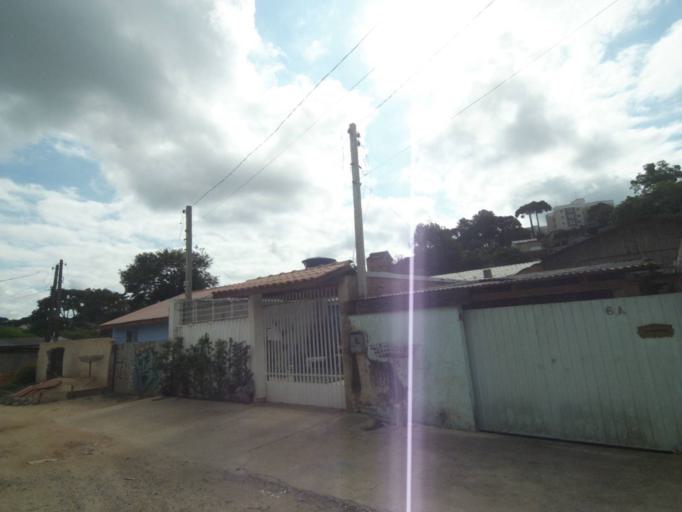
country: BR
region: Parana
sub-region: Almirante Tamandare
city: Almirante Tamandare
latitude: -25.3791
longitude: -49.2999
